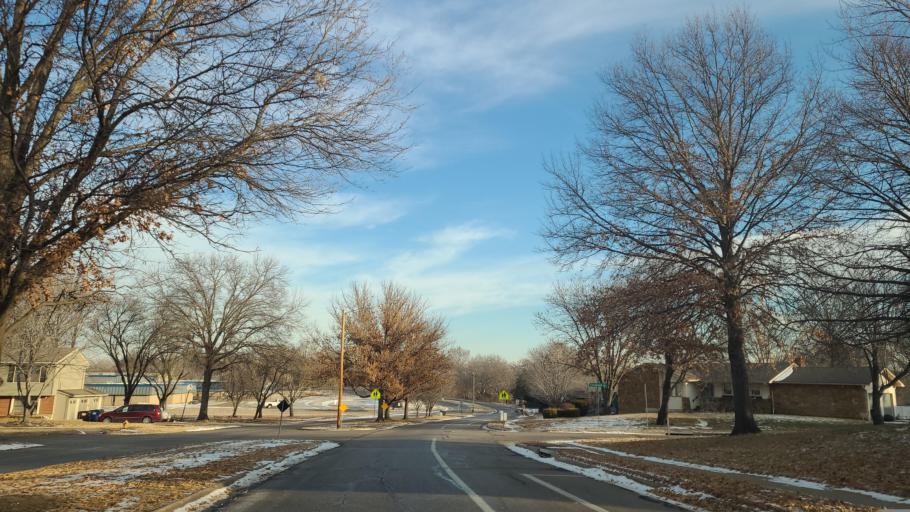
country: US
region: Kansas
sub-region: Douglas County
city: Lawrence
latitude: 38.9806
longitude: -95.2713
